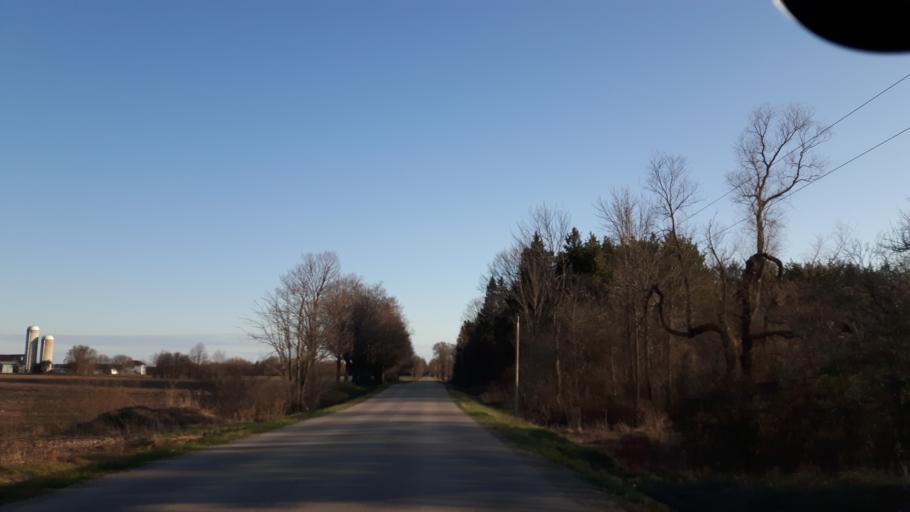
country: CA
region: Ontario
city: Goderich
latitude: 43.6345
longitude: -81.6846
